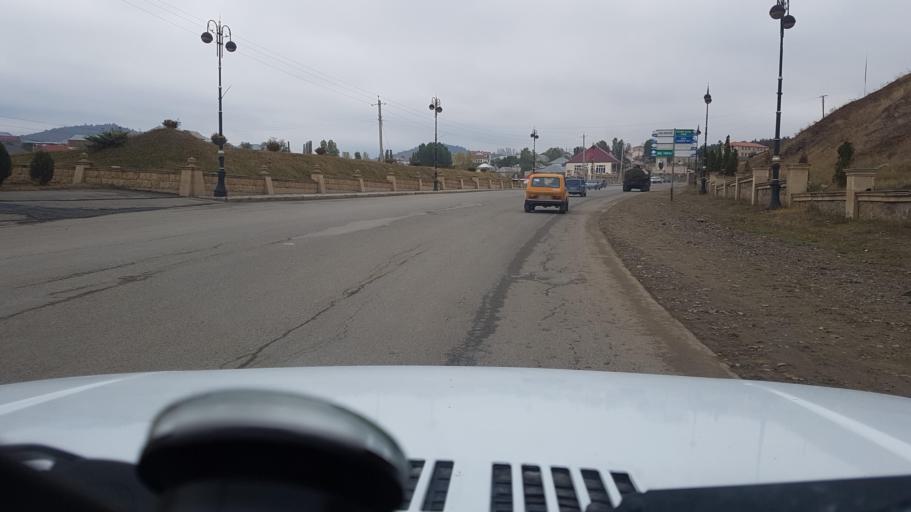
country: AZ
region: Gadabay Rayon
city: Kyadabek
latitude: 40.5843
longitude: 45.8110
